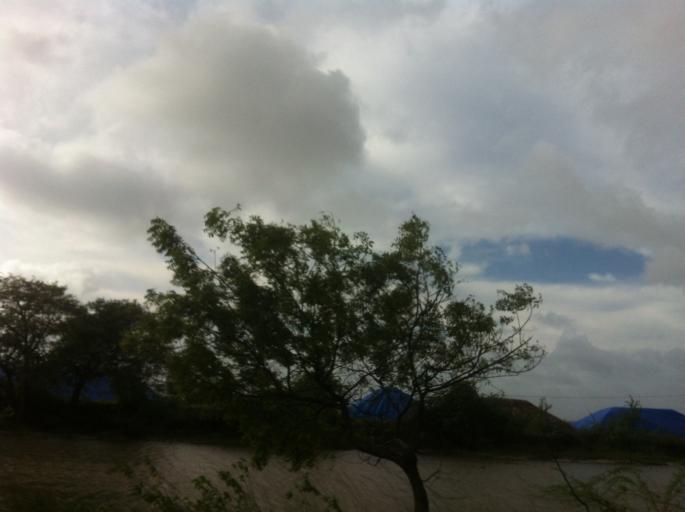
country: IN
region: Tamil Nadu
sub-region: Villupuram
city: Marakkanam
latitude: 12.2071
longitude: 79.9671
